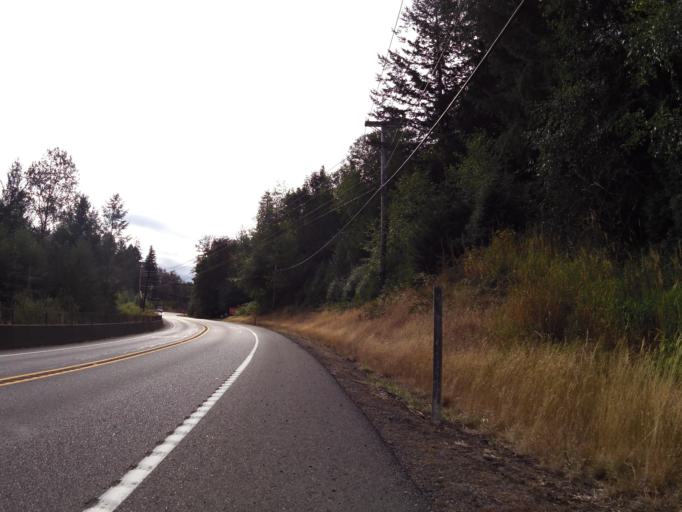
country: US
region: Washington
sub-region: Mason County
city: Allyn
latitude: 47.4021
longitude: -122.8370
